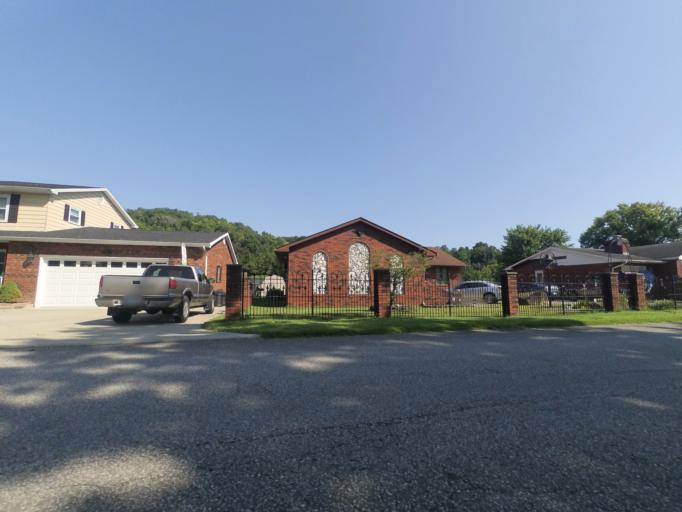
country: US
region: West Virginia
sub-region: Cabell County
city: Huntington
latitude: 38.4428
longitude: -82.4388
